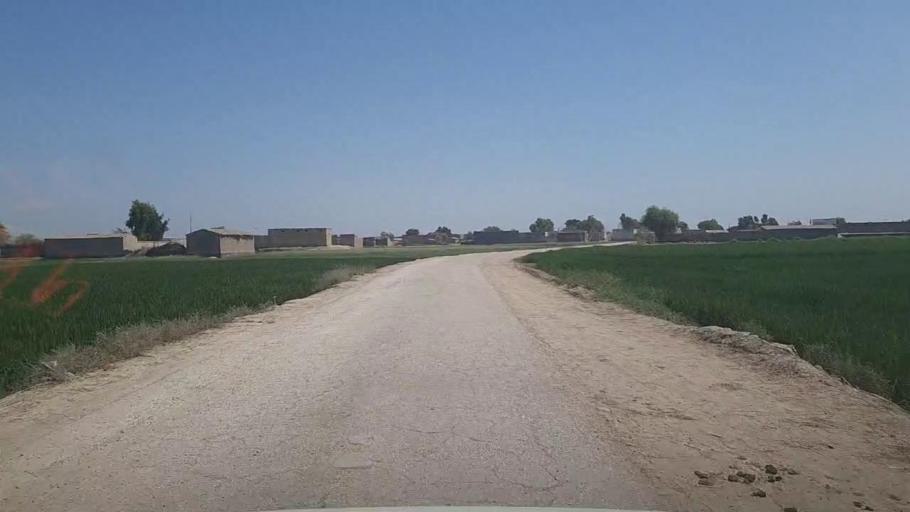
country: PK
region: Sindh
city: Kashmor
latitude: 28.2904
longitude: 69.4352
